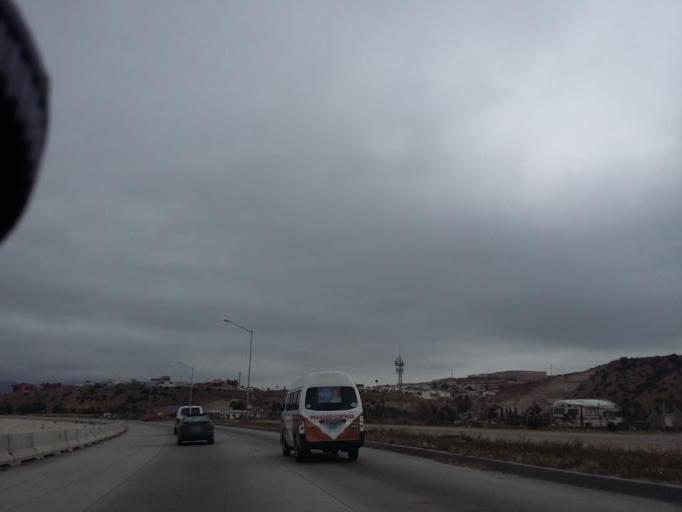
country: MX
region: Baja California
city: Tijuana
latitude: 32.5104
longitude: -116.9442
